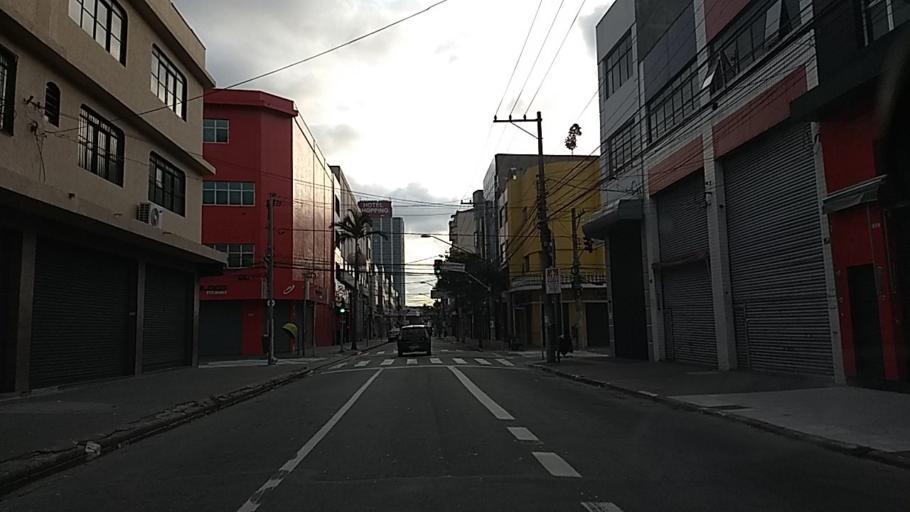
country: BR
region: Sao Paulo
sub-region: Sao Paulo
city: Sao Paulo
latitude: -23.5355
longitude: -46.6174
